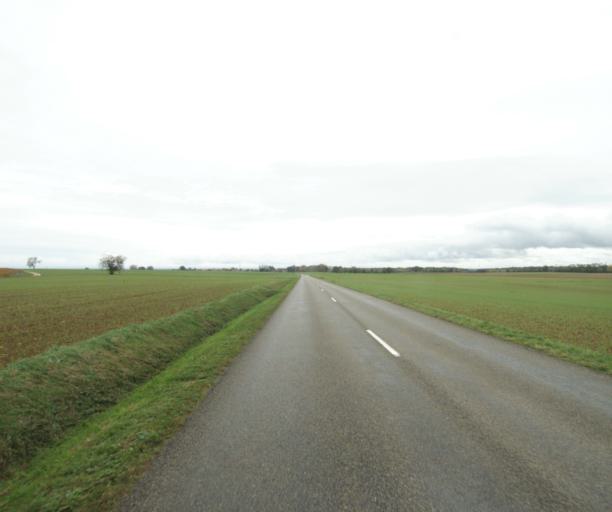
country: FR
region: Bourgogne
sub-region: Departement de Saone-et-Loire
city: Saint-Martin-Belle-Roche
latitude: 46.4676
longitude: 4.8580
